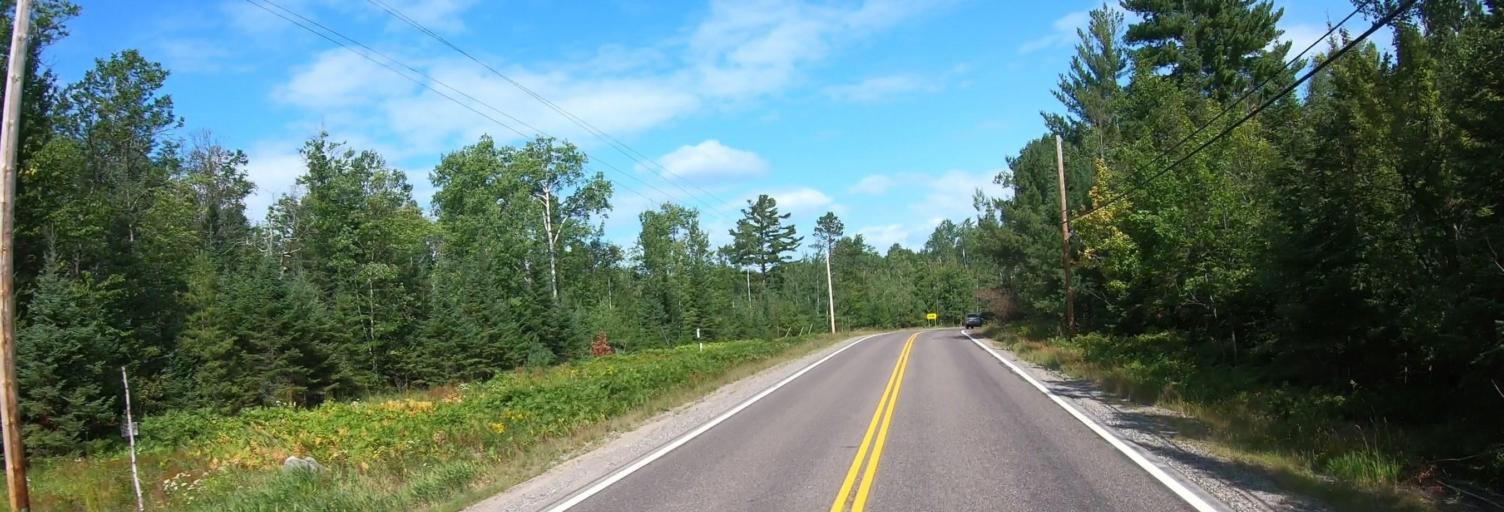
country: US
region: Minnesota
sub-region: Saint Louis County
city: Mountain Iron
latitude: 47.9337
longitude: -92.6759
